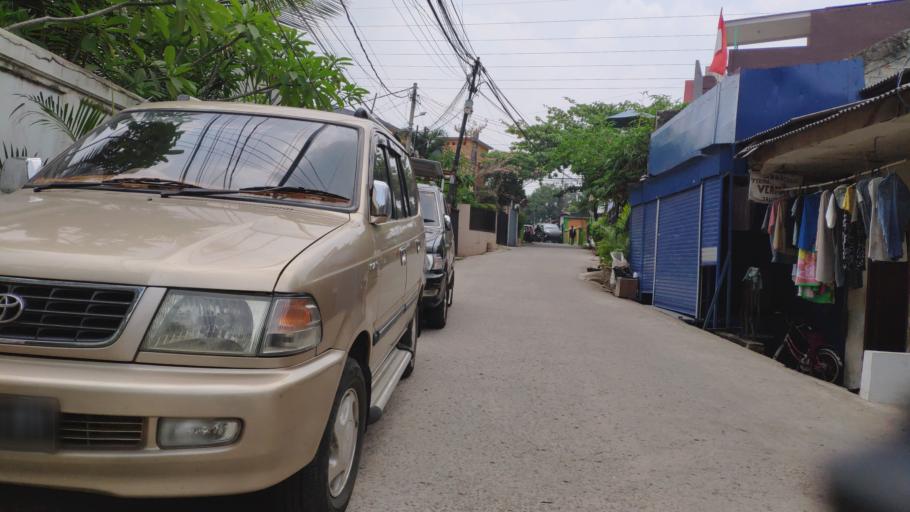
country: ID
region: West Java
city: Depok
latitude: -6.3107
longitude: 106.8293
